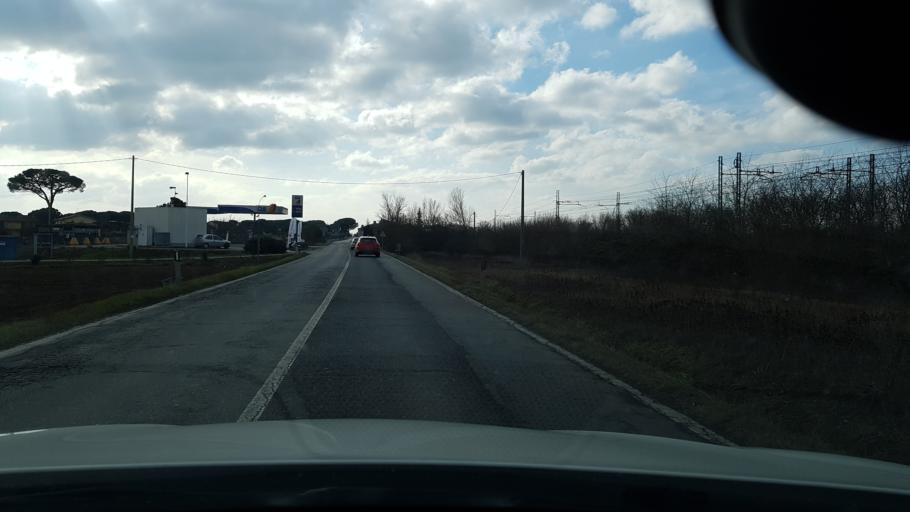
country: IT
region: Tuscany
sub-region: Province of Arezzo
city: Terontola
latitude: 43.1848
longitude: 12.0134
